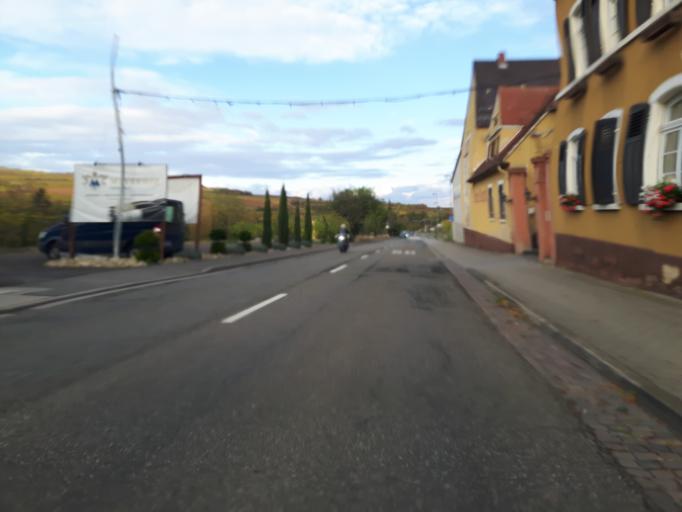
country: DE
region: Rheinland-Pfalz
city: Grunstadt
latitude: 49.5784
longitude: 8.1634
